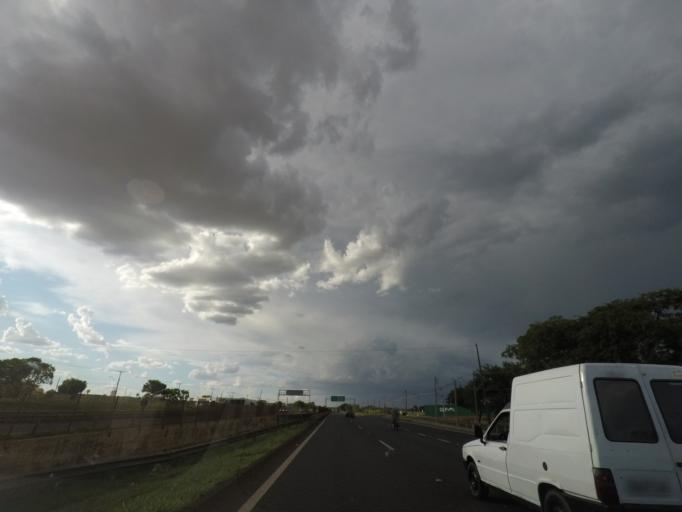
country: BR
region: Sao Paulo
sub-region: Ribeirao Preto
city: Ribeirao Preto
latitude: -21.1231
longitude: -47.7727
